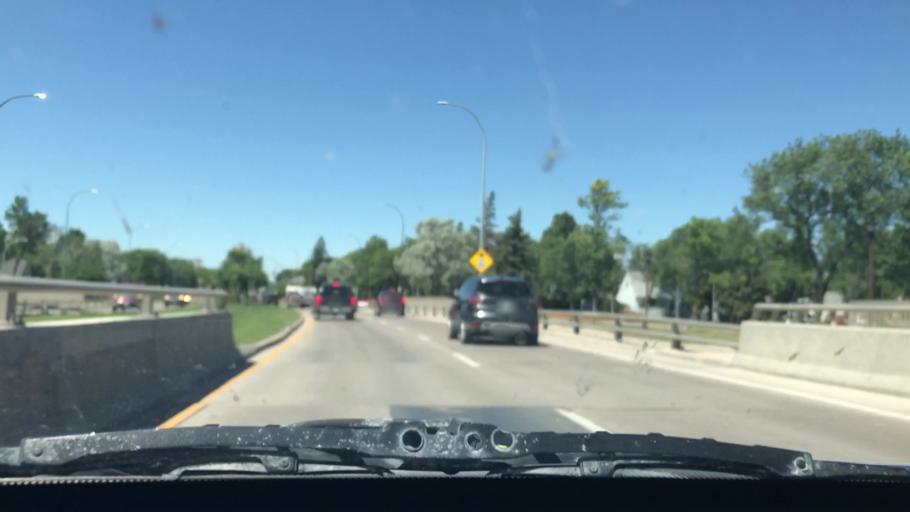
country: CA
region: Manitoba
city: Winnipeg
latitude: 49.8570
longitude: -97.1275
